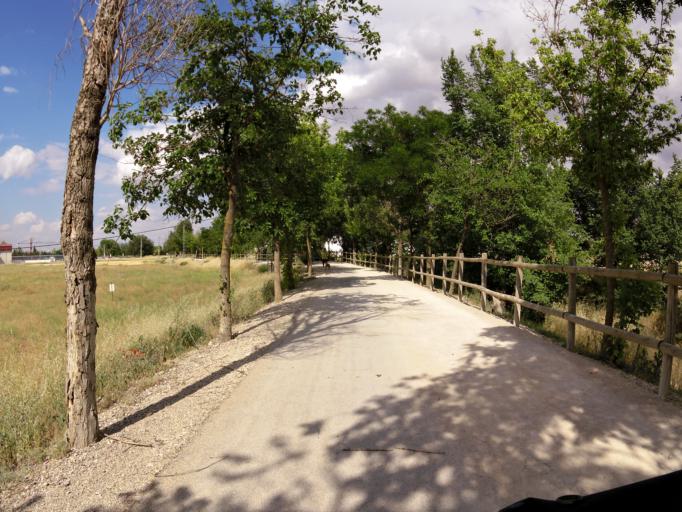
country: ES
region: Castille-La Mancha
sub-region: Provincia de Albacete
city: Albacete
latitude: 38.9955
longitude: -1.8941
